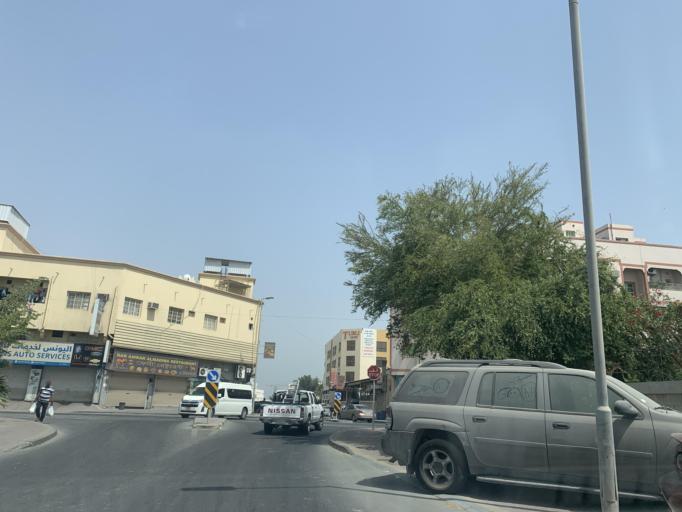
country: BH
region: Northern
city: Madinat `Isa
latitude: 26.1886
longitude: 50.5532
